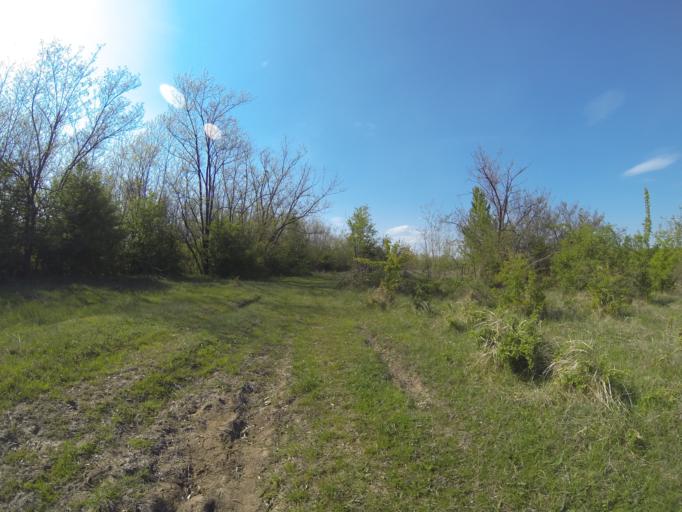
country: RO
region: Gorj
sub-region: Comuna Crusetu
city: Crusetu
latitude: 44.6304
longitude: 23.6368
